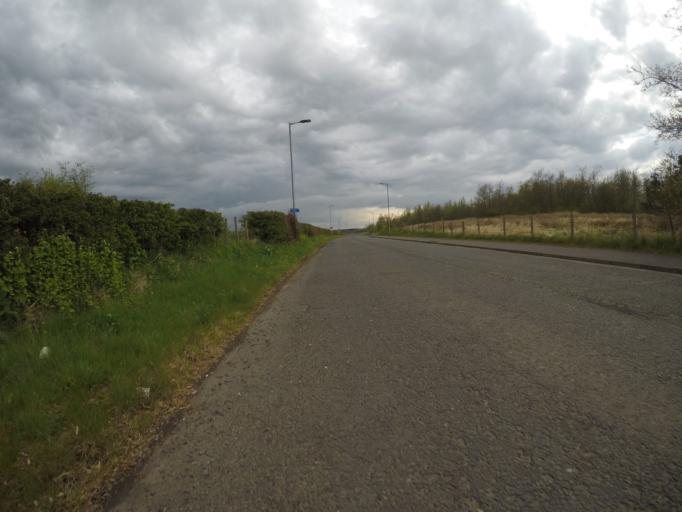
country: GB
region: Scotland
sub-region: East Ayrshire
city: Kilmarnock
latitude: 55.6508
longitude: -4.4493
